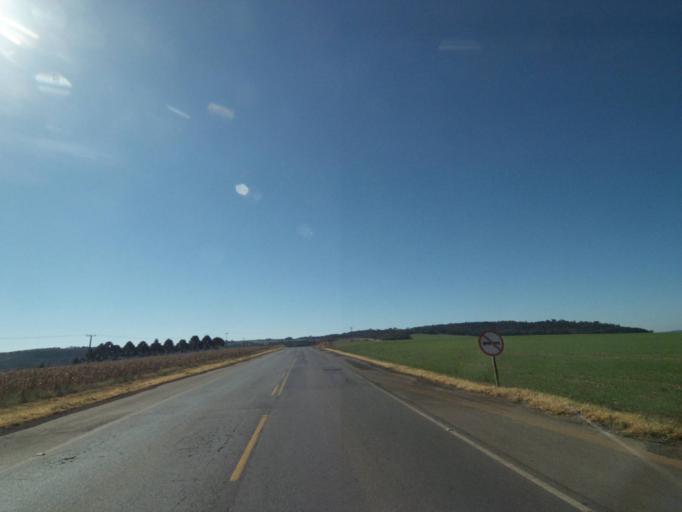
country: BR
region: Parana
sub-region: Tibagi
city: Tibagi
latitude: -24.3873
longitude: -50.3342
